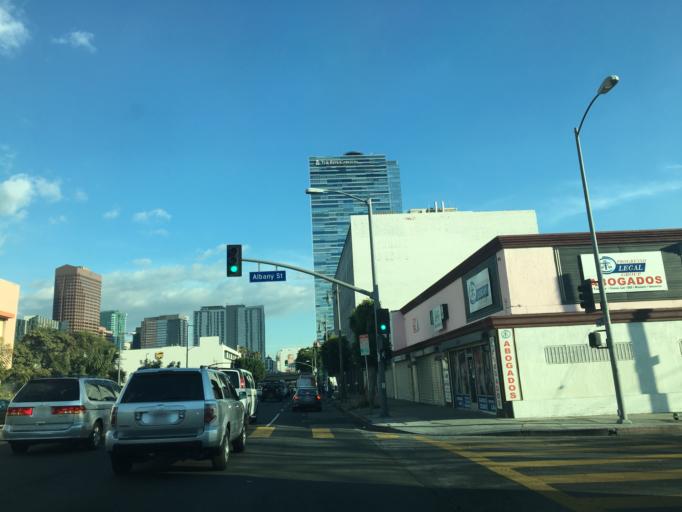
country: US
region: California
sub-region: Los Angeles County
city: Los Angeles
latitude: 34.0478
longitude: -118.2712
